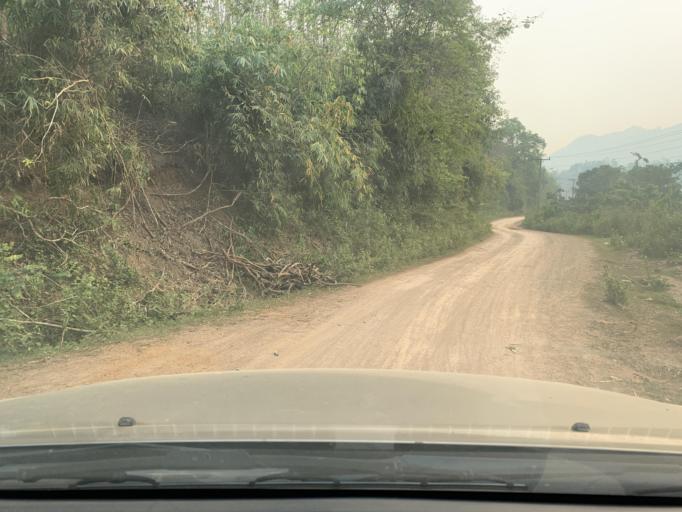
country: LA
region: Louangphabang
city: Louangphabang
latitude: 19.9276
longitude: 102.0774
